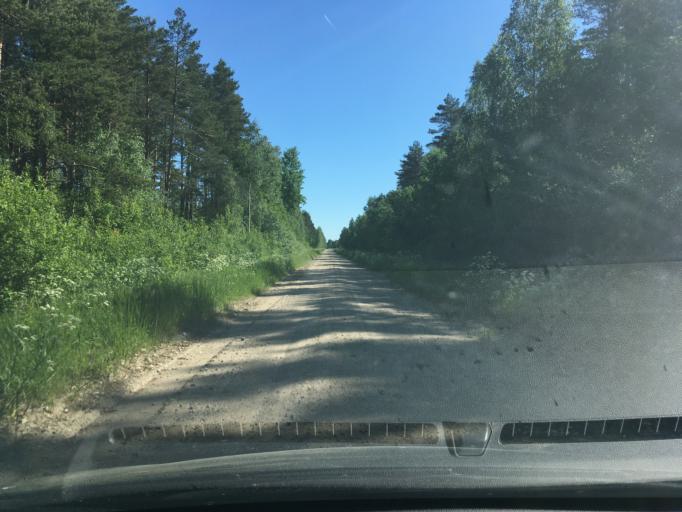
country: EE
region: Laeaene
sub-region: Lihula vald
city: Lihula
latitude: 58.6403
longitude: 23.7655
